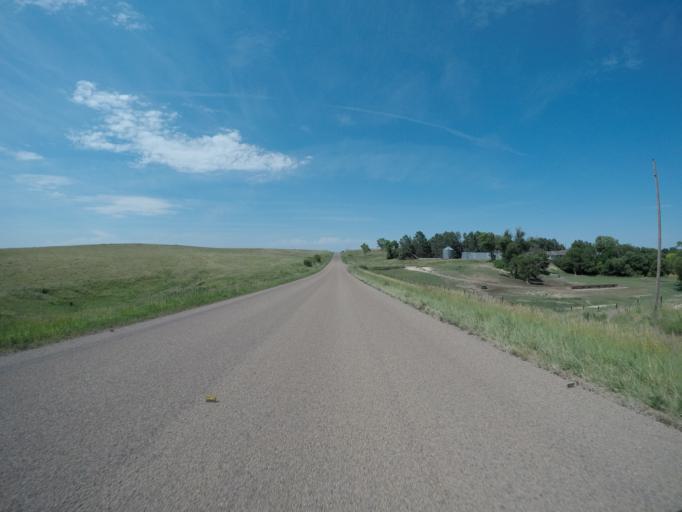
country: US
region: Nebraska
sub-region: Webster County
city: Red Cloud
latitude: 40.0396
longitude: -98.3303
